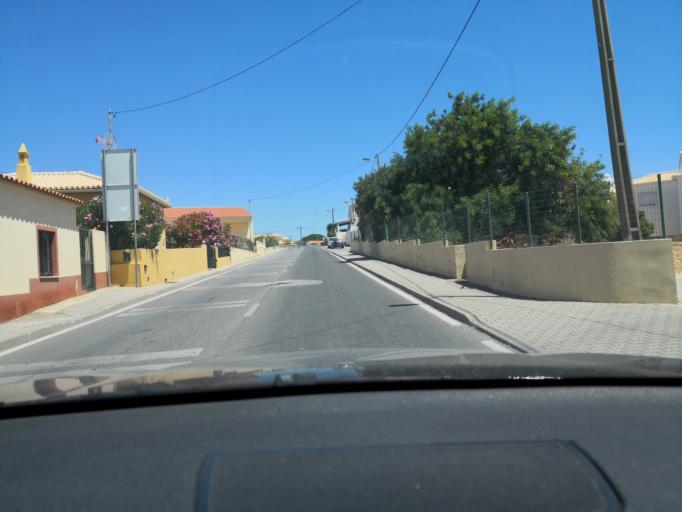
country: PT
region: Faro
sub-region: Albufeira
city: Ferreiras
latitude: 37.1024
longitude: -8.2154
